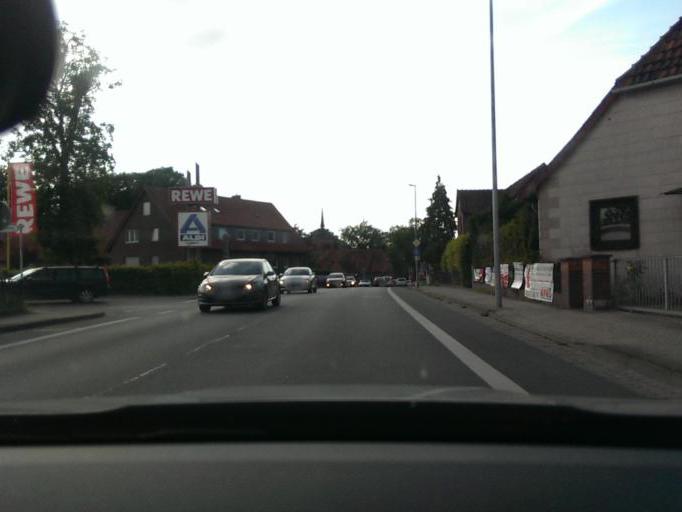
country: DE
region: Lower Saxony
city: Elze
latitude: 52.5448
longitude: 9.7363
